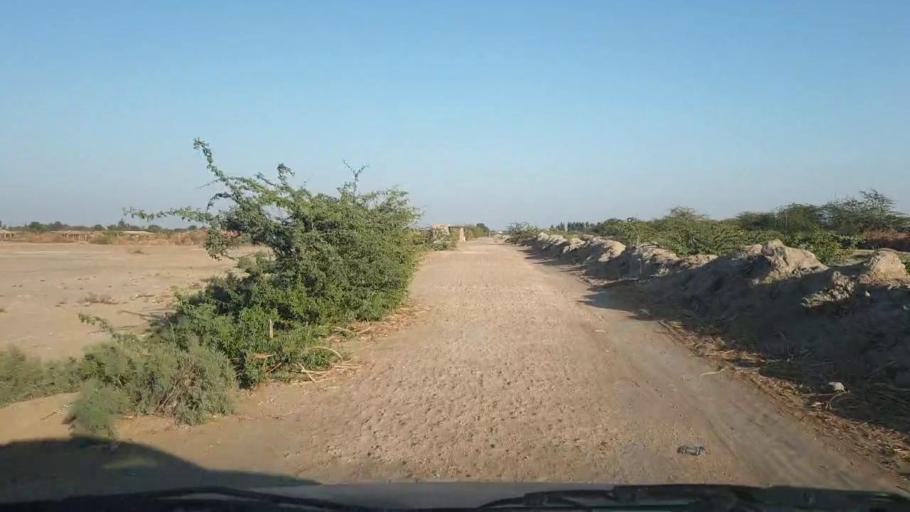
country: PK
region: Sindh
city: Samaro
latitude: 25.3190
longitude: 69.3003
